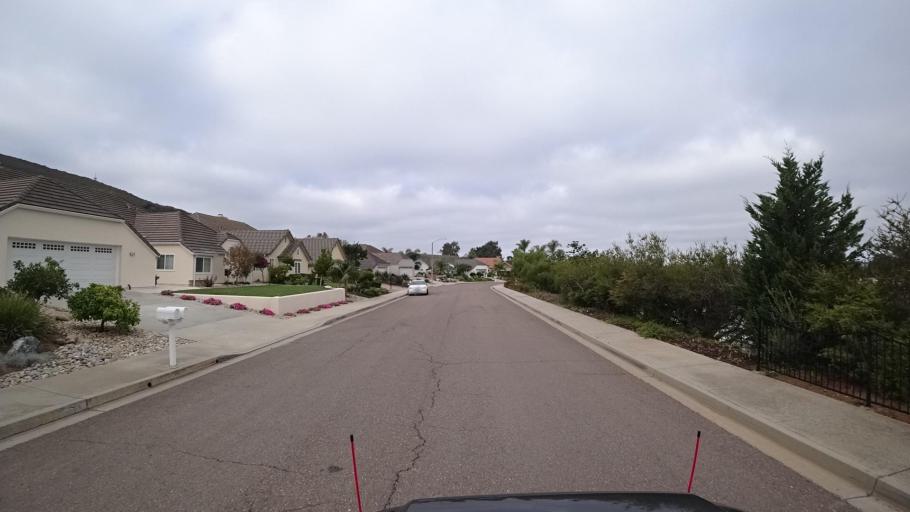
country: US
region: California
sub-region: San Diego County
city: Lake San Marcos
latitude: 33.1185
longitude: -117.1945
